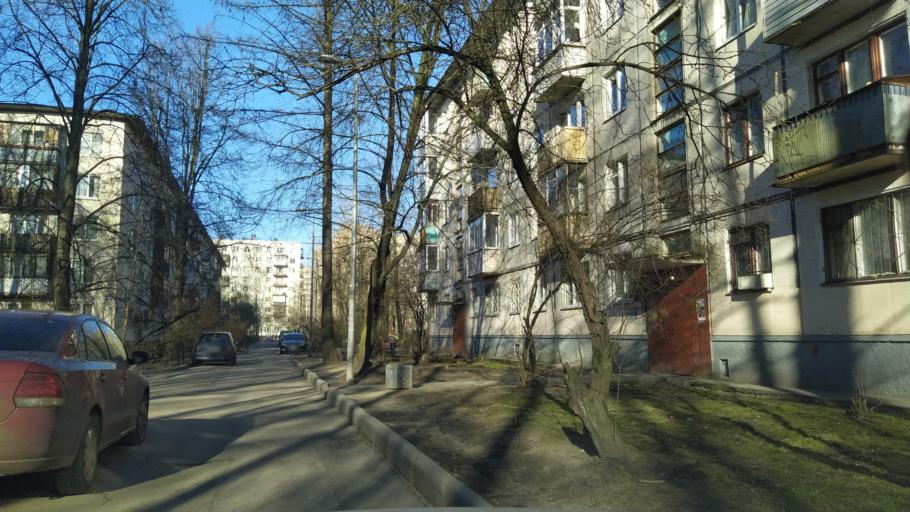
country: RU
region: Leningrad
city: Akademicheskoe
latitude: 60.0136
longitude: 30.4067
